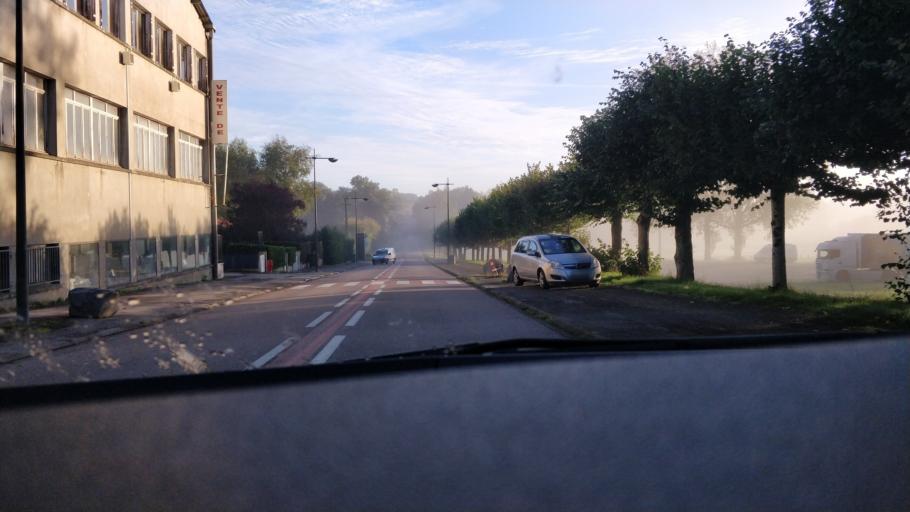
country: FR
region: Limousin
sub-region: Departement de la Haute-Vienne
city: Sauviat-sur-Vige
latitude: 45.9089
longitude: 1.6139
